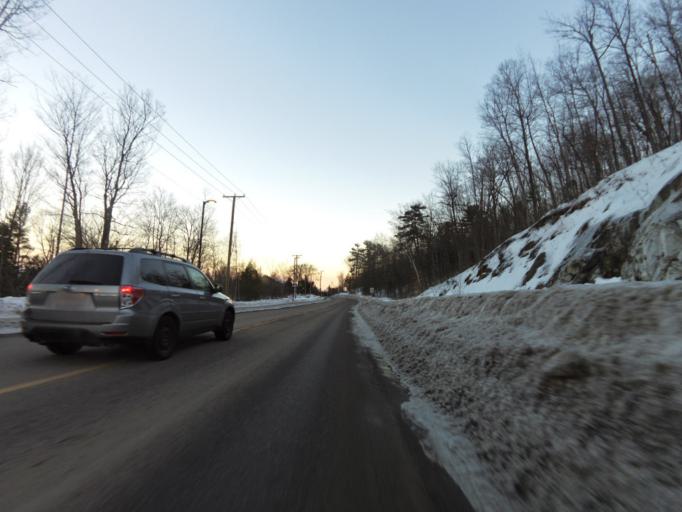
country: CA
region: Quebec
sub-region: Outaouais
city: Gatineau
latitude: 45.4761
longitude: -75.7877
